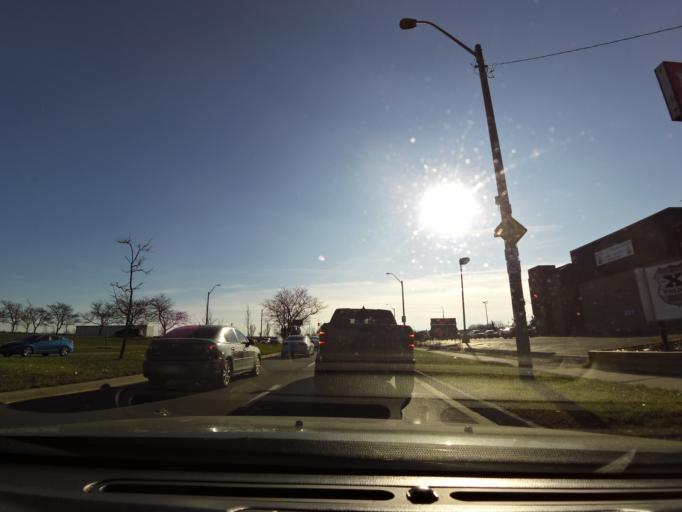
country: CA
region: Ontario
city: Hamilton
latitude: 43.2160
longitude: -79.8652
